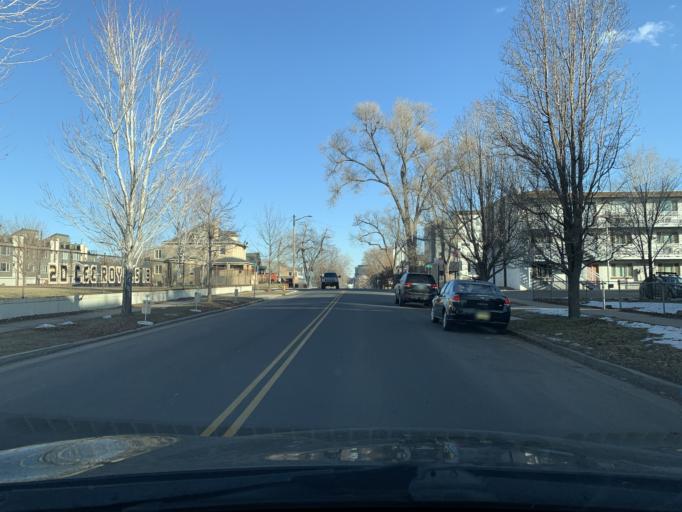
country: US
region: Colorado
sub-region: Denver County
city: Denver
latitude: 39.7548
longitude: -105.0214
